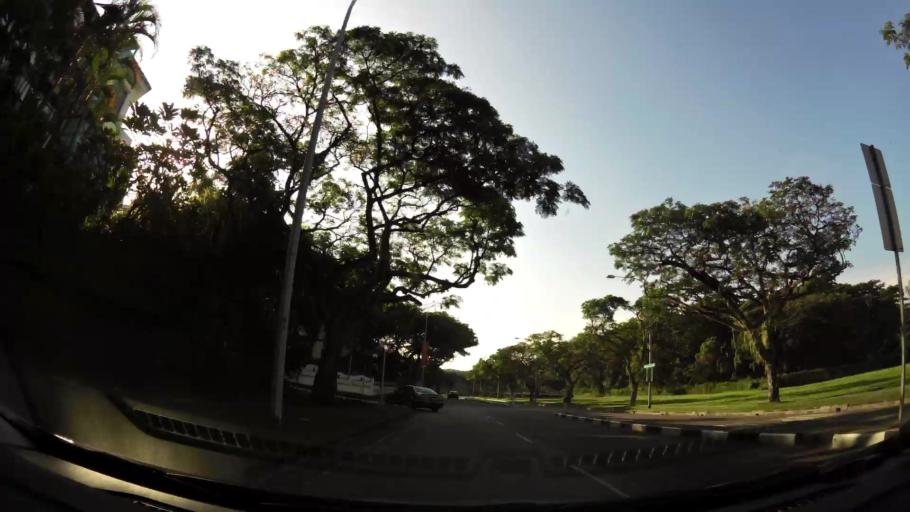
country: SG
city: Singapore
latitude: 1.3190
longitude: 103.9477
